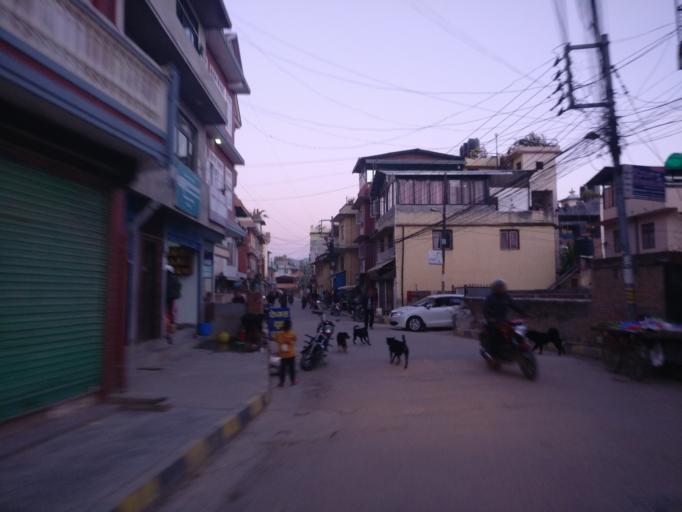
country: NP
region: Central Region
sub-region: Bagmati Zone
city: Patan
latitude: 27.6542
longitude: 85.3199
